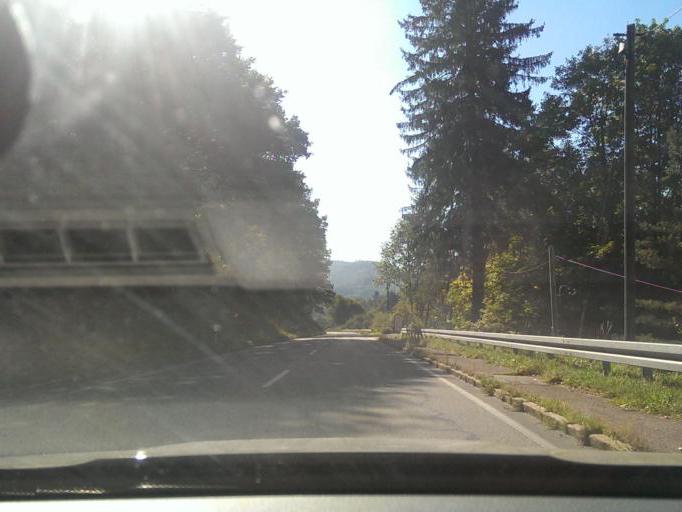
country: DE
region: Baden-Wuerttemberg
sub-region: Karlsruhe Region
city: Bad Herrenalb
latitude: 48.8146
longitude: 8.4450
